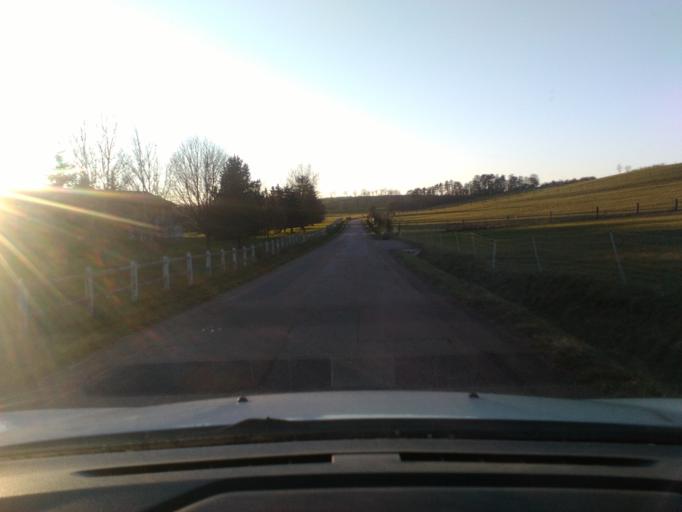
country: FR
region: Lorraine
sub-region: Departement des Vosges
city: Mirecourt
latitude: 48.2975
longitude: 6.1060
